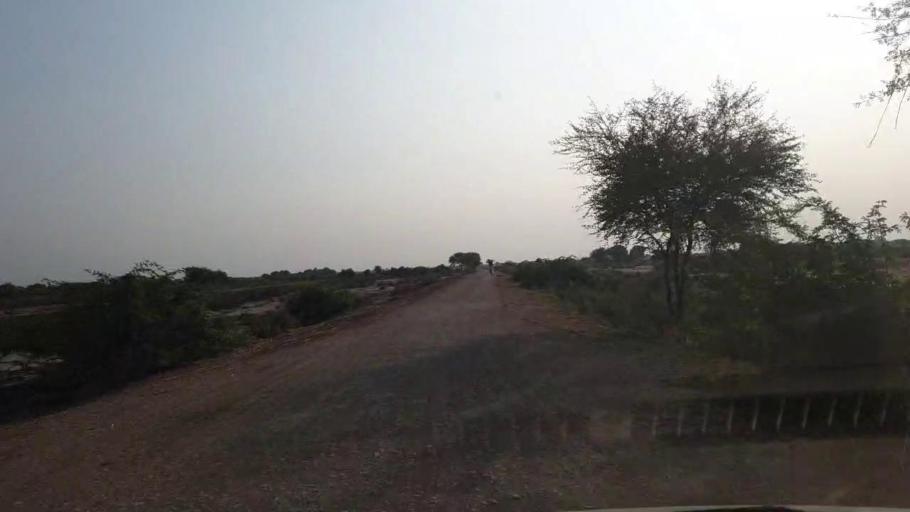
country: PK
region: Sindh
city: Rajo Khanani
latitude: 25.0118
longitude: 68.7870
